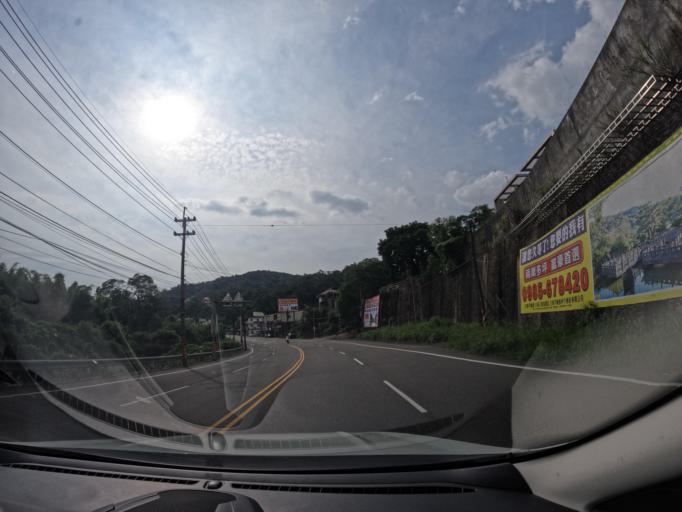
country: TW
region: Taiwan
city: Daxi
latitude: 24.8947
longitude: 121.3156
